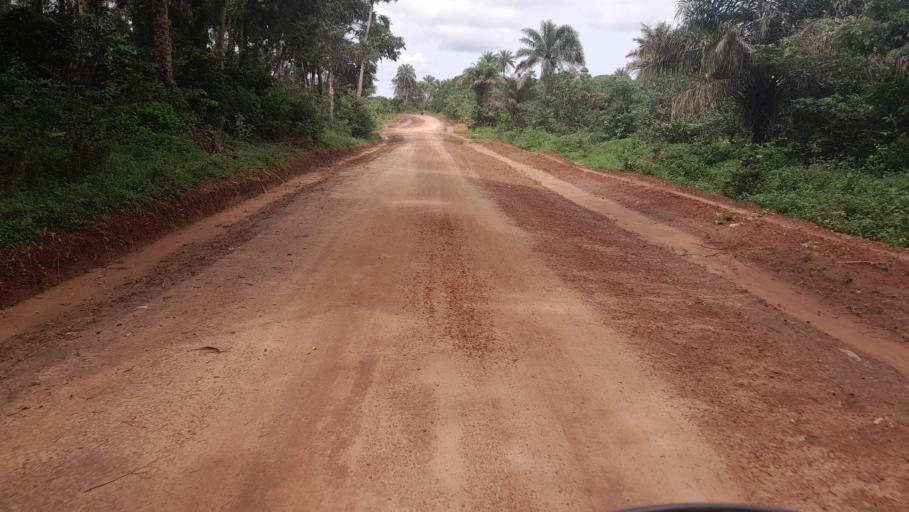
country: GN
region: Boke
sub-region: Boffa
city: Boffa
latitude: 10.0754
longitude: -13.8669
